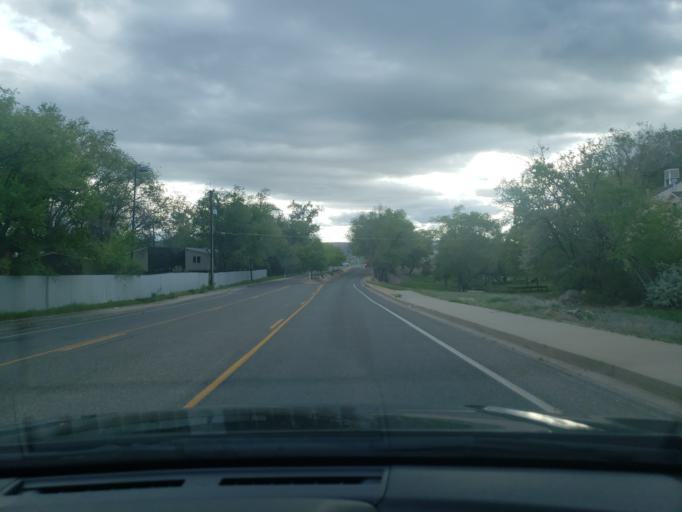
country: US
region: Colorado
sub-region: Mesa County
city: Orchard Mesa
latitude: 39.0486
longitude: -108.5635
